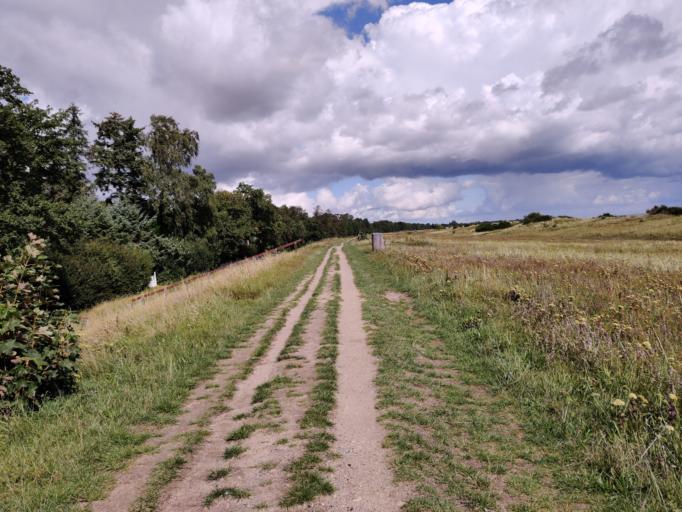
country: DK
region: Zealand
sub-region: Guldborgsund Kommune
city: Nykobing Falster
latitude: 54.6942
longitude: 11.9716
